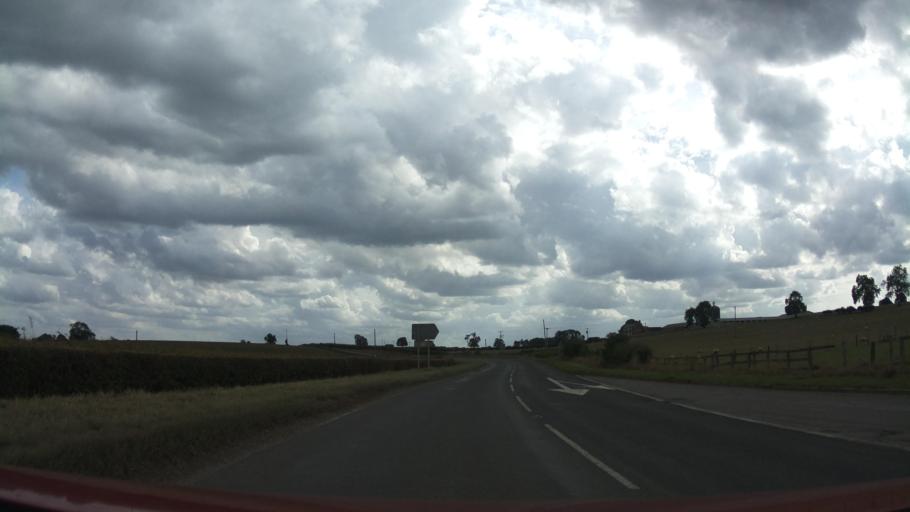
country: GB
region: England
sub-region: North Yorkshire
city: Ripon
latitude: 54.1753
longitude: -1.5531
